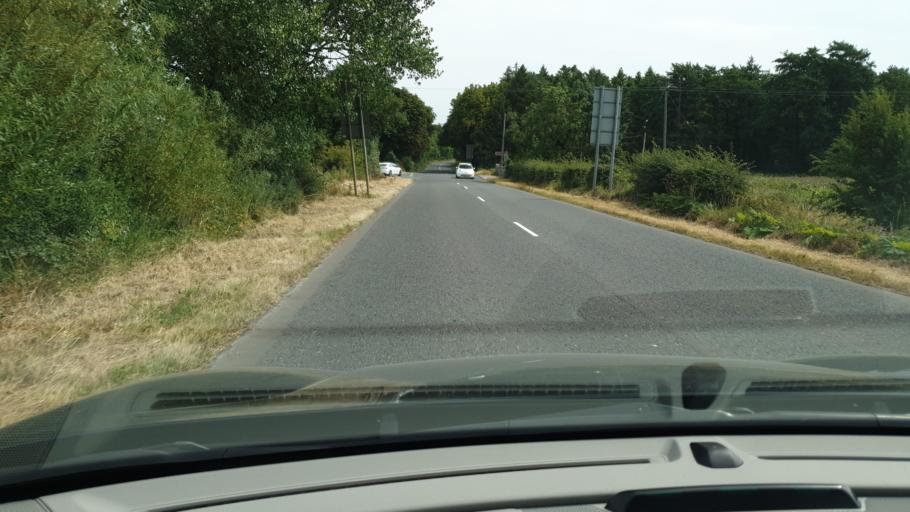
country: IE
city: Kentstown
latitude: 53.6259
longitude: -6.5258
